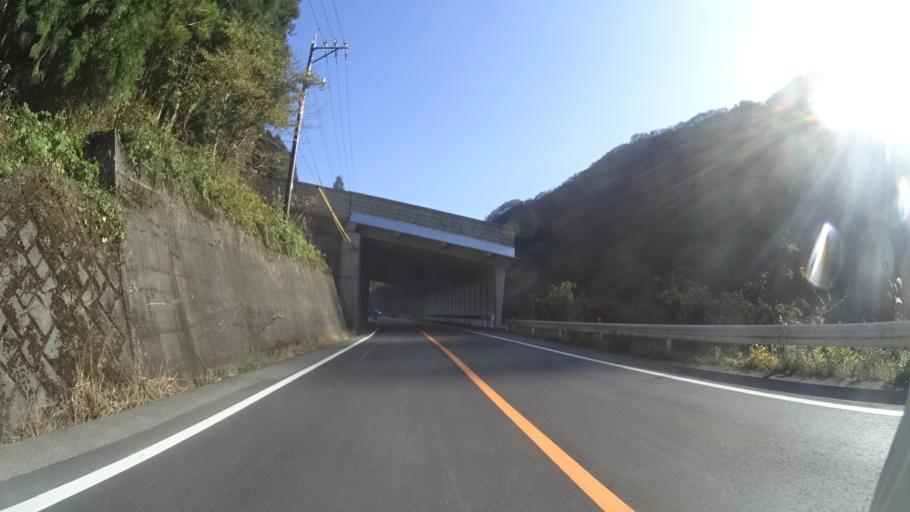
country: JP
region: Fukui
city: Ono
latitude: 35.9126
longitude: 136.6280
